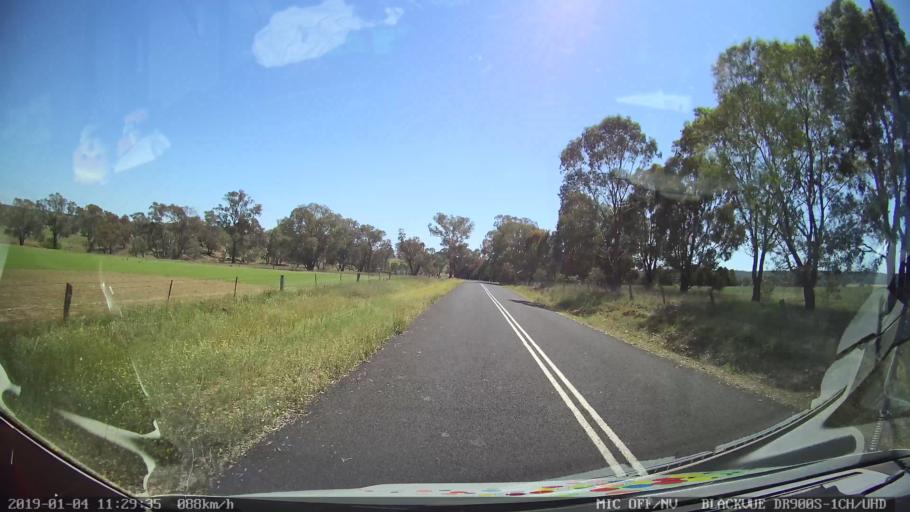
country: AU
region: New South Wales
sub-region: Cabonne
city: Molong
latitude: -33.0861
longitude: 148.7752
